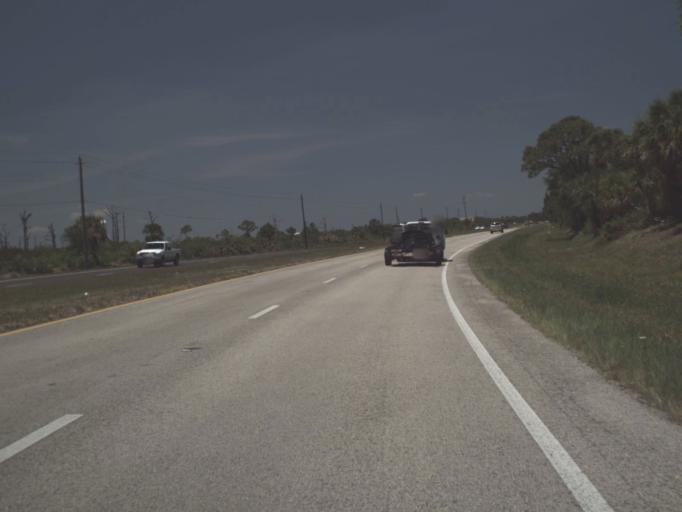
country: US
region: Florida
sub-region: Brevard County
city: Malabar
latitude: 27.9719
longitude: -80.5476
